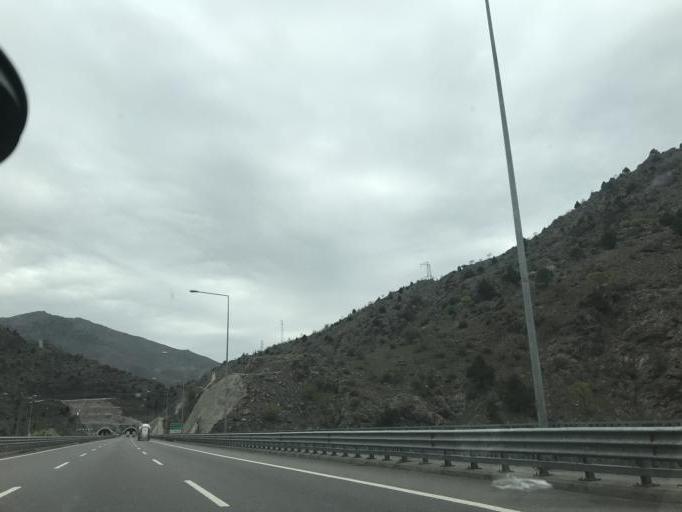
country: TR
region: Nigde
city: Ciftehan
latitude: 37.5541
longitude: 34.7726
